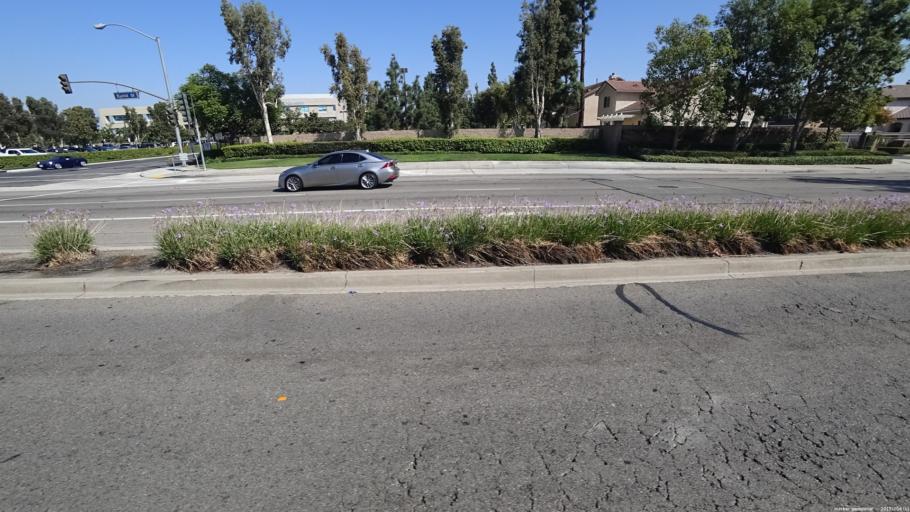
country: US
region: California
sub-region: Orange County
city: Garden Grove
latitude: 33.7862
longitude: -117.9412
